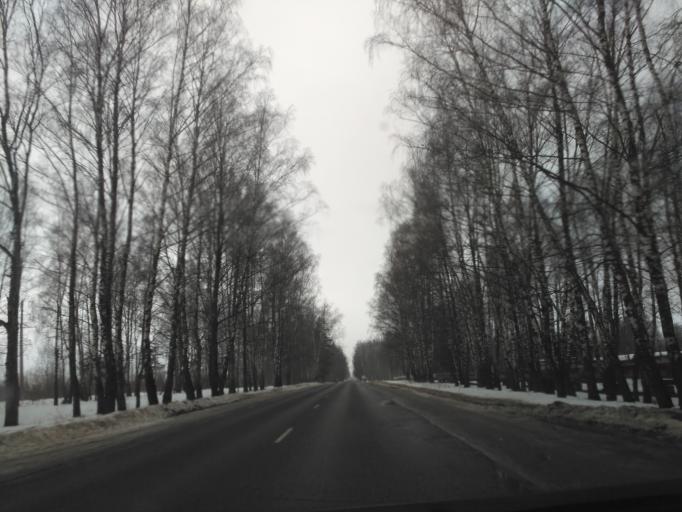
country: BY
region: Minsk
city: Horad Zhodzina
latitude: 54.0878
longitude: 28.3230
